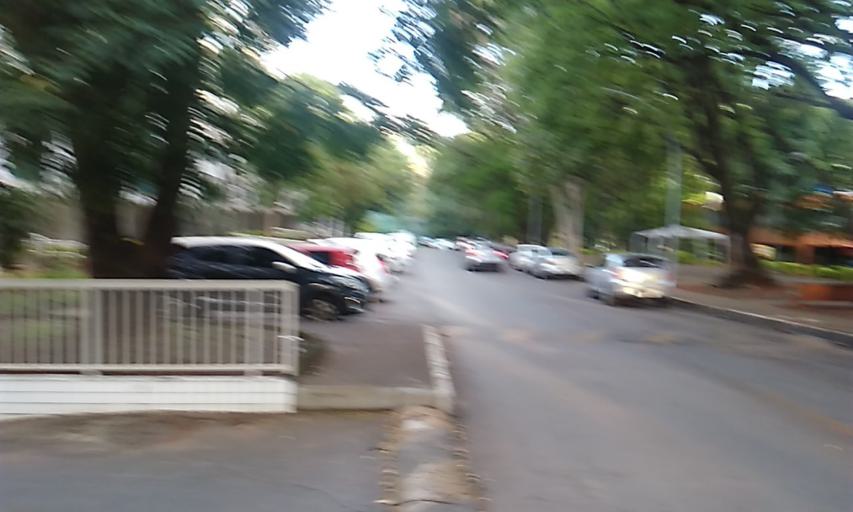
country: BR
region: Federal District
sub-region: Brasilia
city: Brasilia
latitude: -15.7767
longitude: -47.8834
